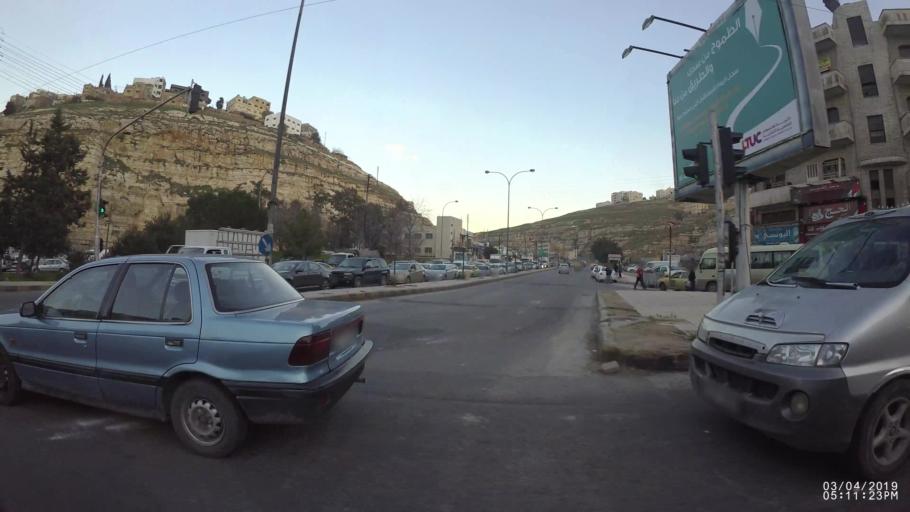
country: JO
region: Amman
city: Al Quwaysimah
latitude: 31.9311
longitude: 35.9215
